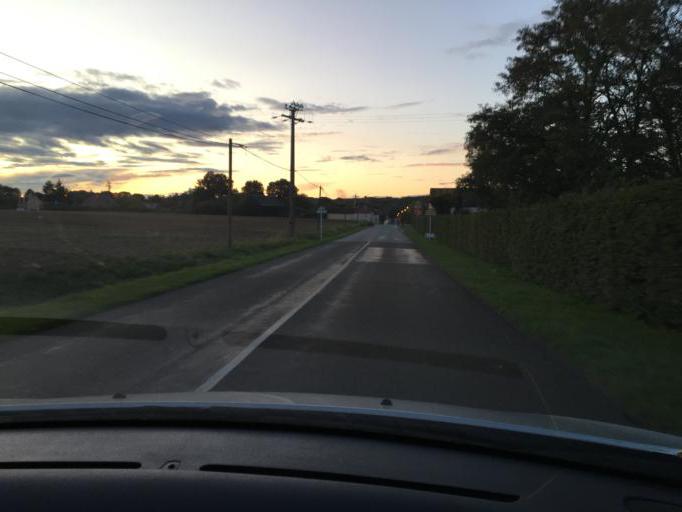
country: FR
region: Centre
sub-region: Departement d'Eure-et-Loir
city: Unverre
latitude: 48.2591
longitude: 1.1034
